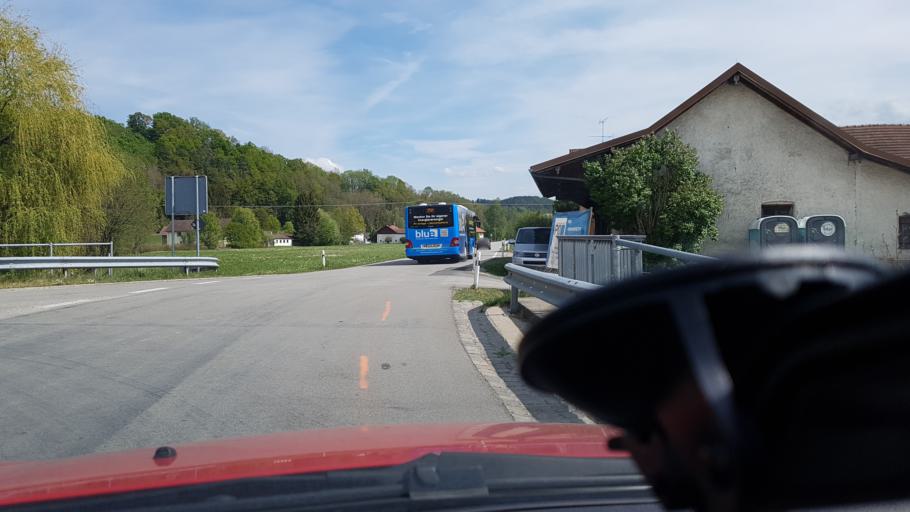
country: DE
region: Bavaria
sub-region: Lower Bavaria
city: Ering
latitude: 48.3265
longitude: 13.1261
